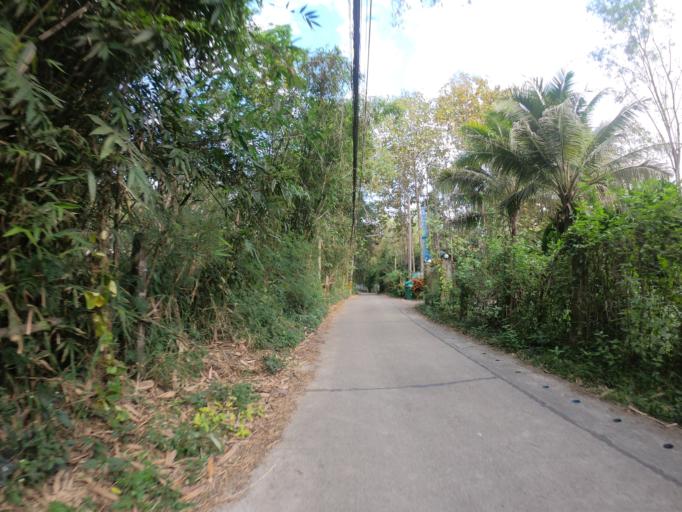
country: TH
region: Chiang Mai
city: Chiang Mai
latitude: 18.8243
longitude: 98.9511
